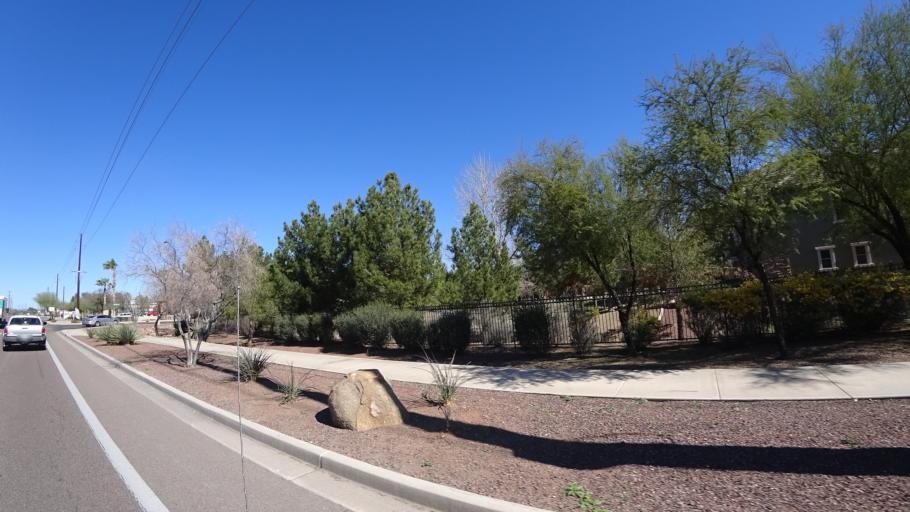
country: US
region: Arizona
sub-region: Maricopa County
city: Gilbert
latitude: 33.3024
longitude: -111.7554
